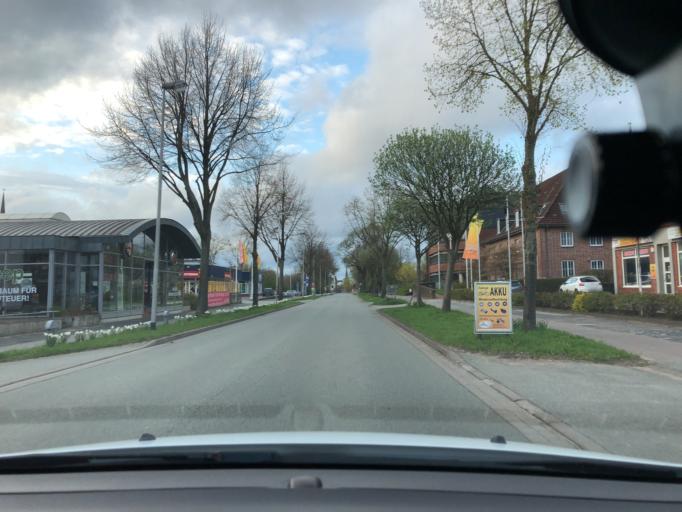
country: DE
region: Schleswig-Holstein
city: Flensburg
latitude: 54.7717
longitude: 9.4352
